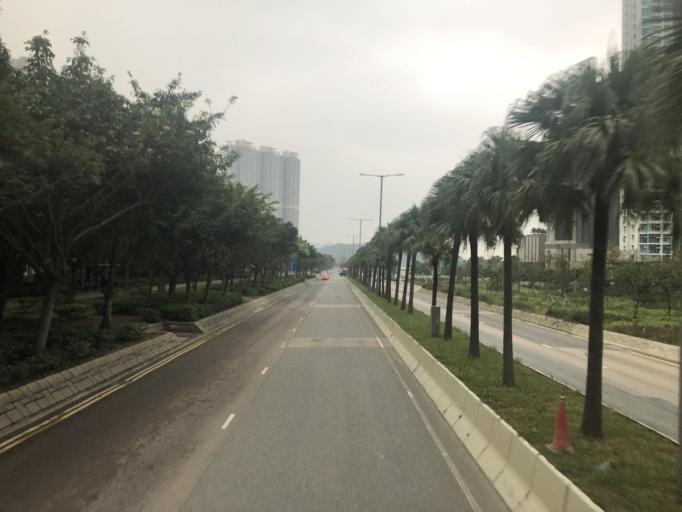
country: HK
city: Tai O
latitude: 22.2943
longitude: 113.9490
